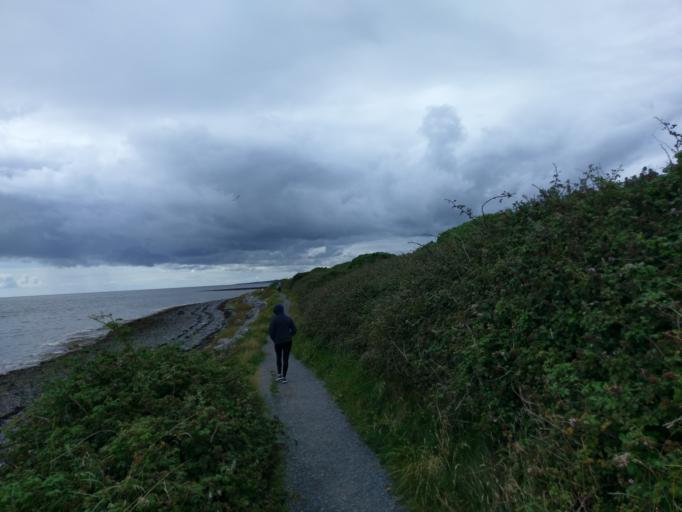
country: IE
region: Connaught
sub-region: County Galway
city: Oranmore
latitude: 53.2459
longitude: -8.9815
